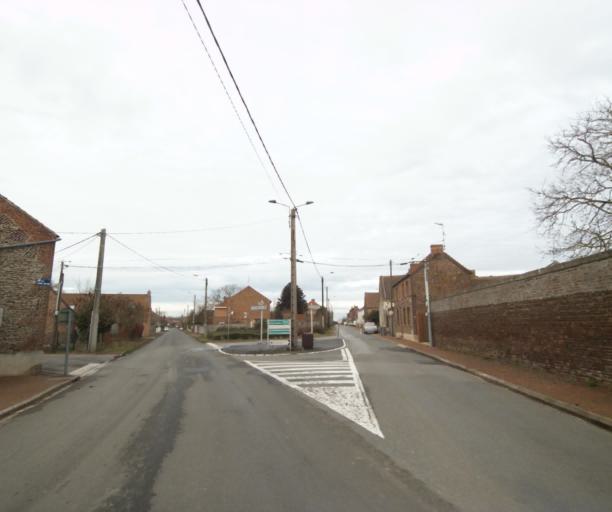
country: FR
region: Nord-Pas-de-Calais
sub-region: Departement du Nord
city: Hergnies
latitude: 50.4776
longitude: 3.5207
